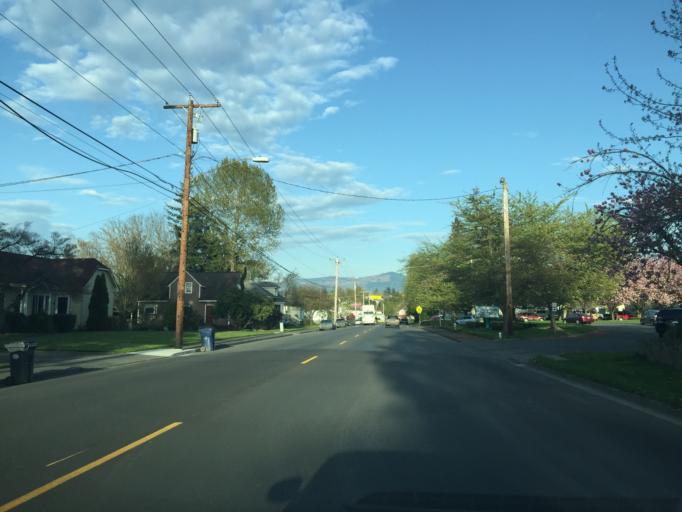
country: US
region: Washington
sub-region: Skagit County
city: Mount Vernon
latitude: 48.4209
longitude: -122.3497
